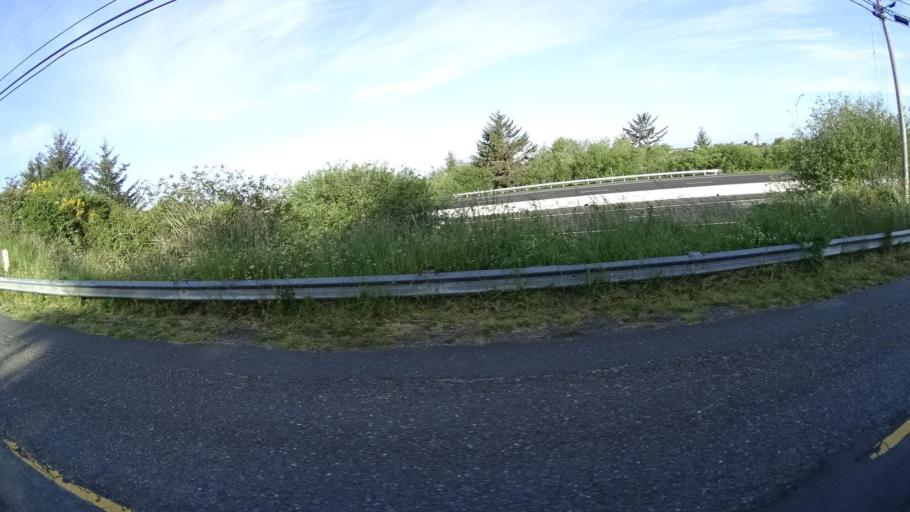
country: US
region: California
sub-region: Humboldt County
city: Humboldt Hill
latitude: 40.7331
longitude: -124.2127
